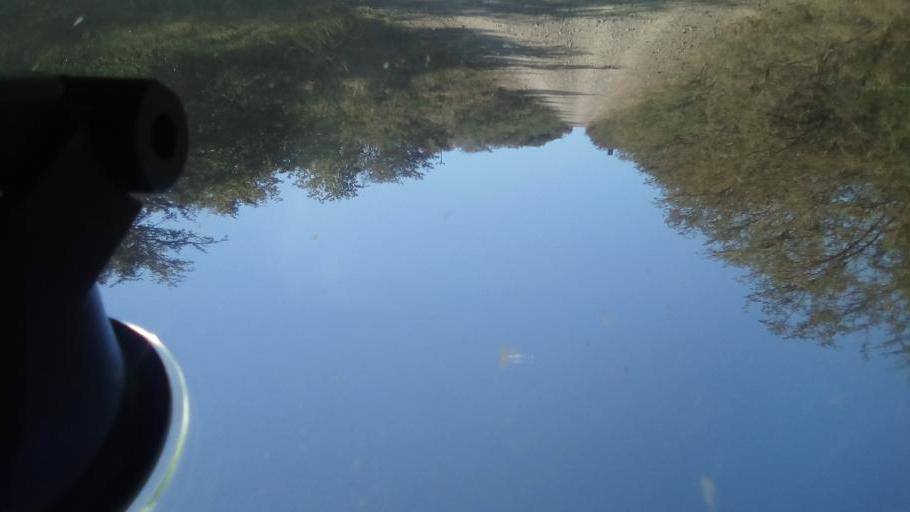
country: ZA
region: Eastern Cape
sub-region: Buffalo City Metropolitan Municipality
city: Bhisho
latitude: -32.7536
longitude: 27.3382
